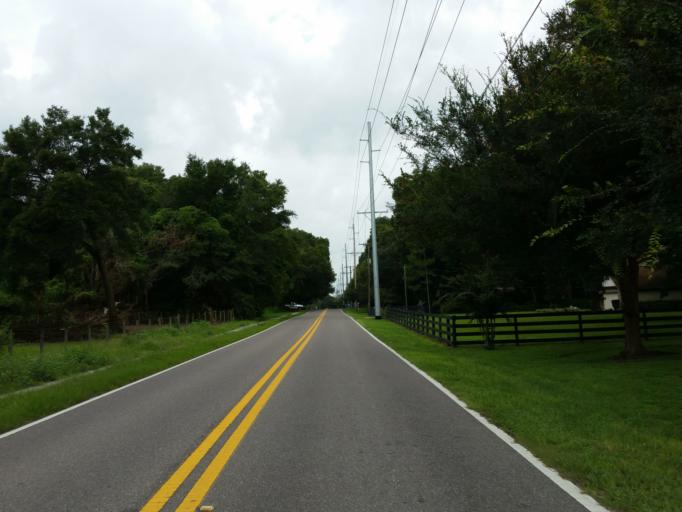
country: US
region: Florida
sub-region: Hillsborough County
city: Thonotosassa
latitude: 28.0508
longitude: -82.2918
